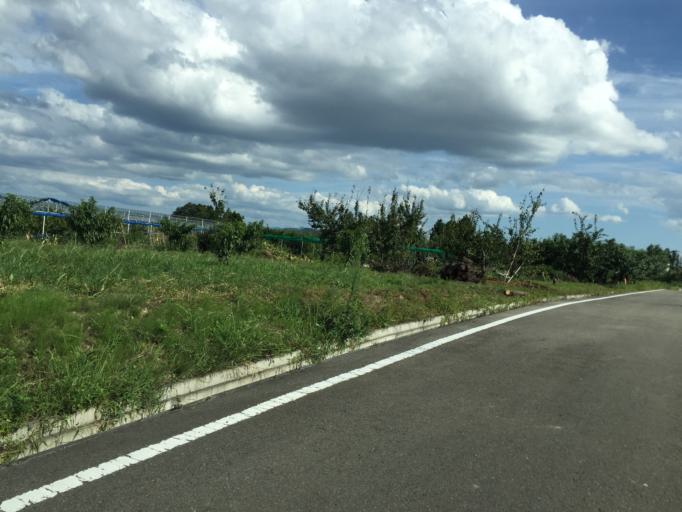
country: JP
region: Fukushima
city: Fukushima-shi
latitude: 37.7997
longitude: 140.4119
